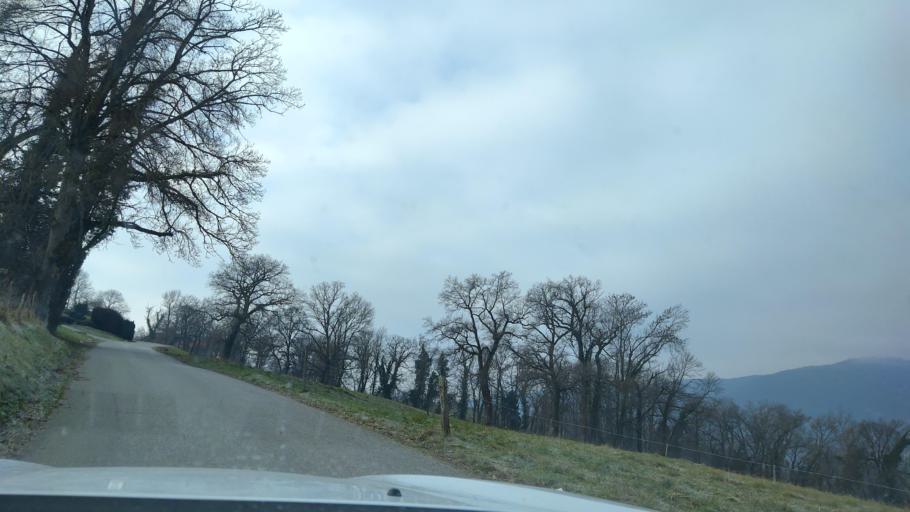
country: FR
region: Rhone-Alpes
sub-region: Departement de la Savoie
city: La Biolle
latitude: 45.7492
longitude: 5.9463
